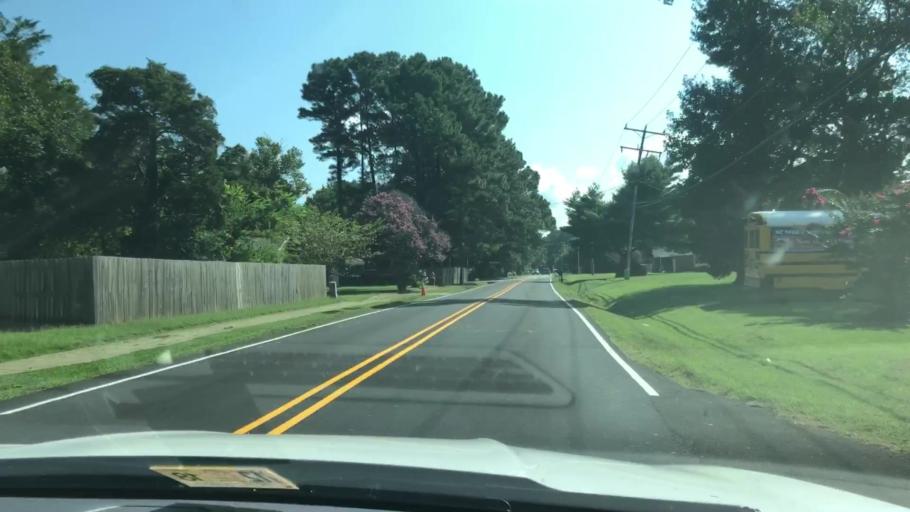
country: US
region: Virginia
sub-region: City of Poquoson
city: Poquoson
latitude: 37.1261
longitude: -76.4503
